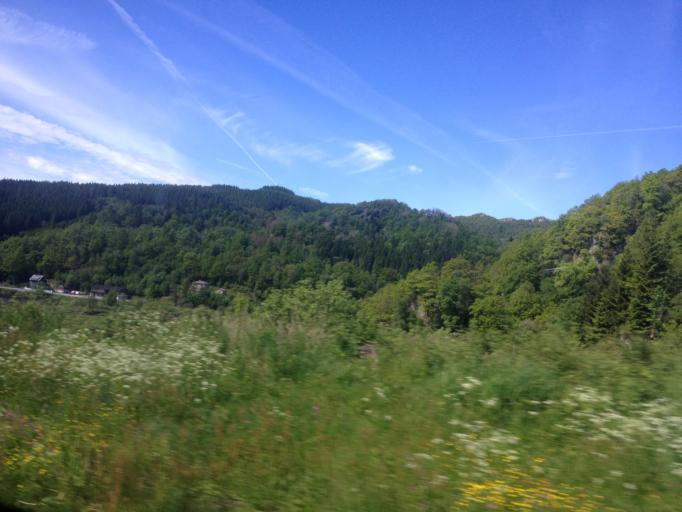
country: NO
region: Rogaland
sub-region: Bjerkreim
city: Vikesa
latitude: 58.5379
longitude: 6.1681
